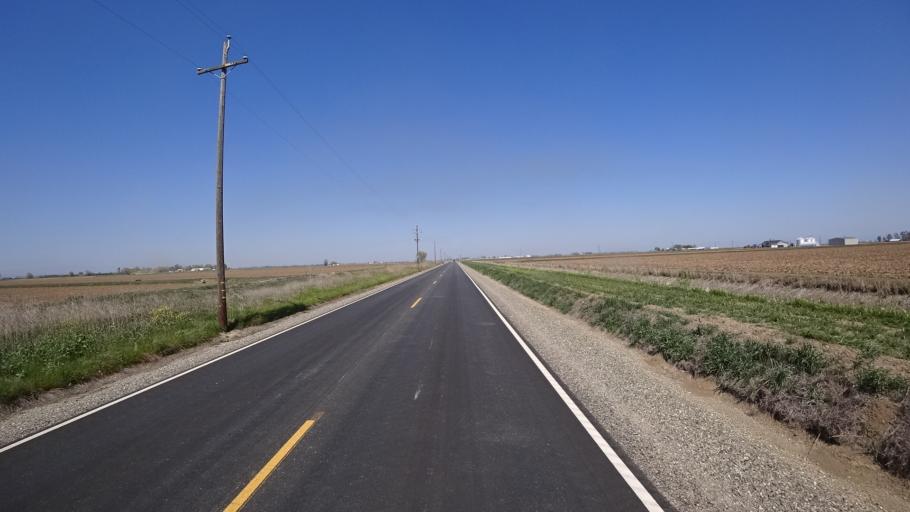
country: US
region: California
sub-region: Glenn County
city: Willows
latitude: 39.4844
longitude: -122.1367
